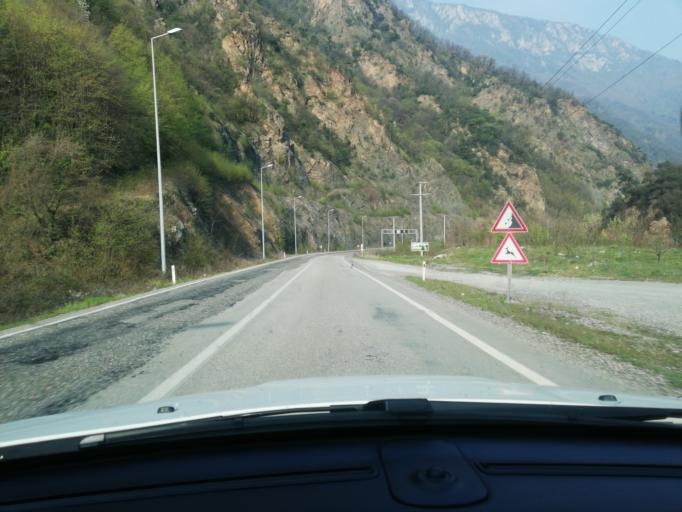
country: TR
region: Karabuk
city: Yenice
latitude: 41.1585
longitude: 32.4626
